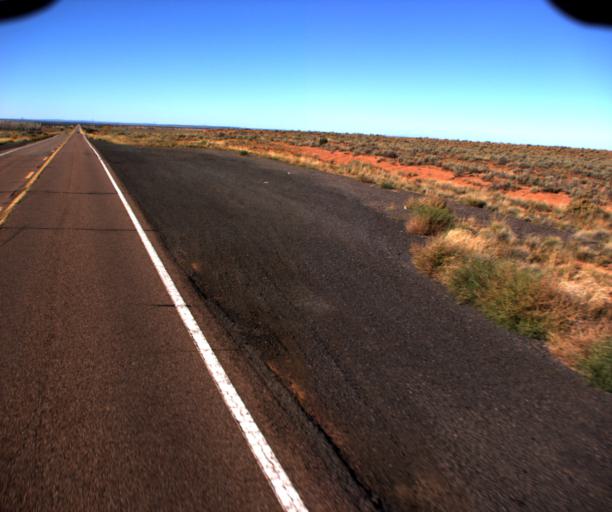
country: US
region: Arizona
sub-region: Navajo County
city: Heber-Overgaard
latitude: 34.6253
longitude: -110.3663
